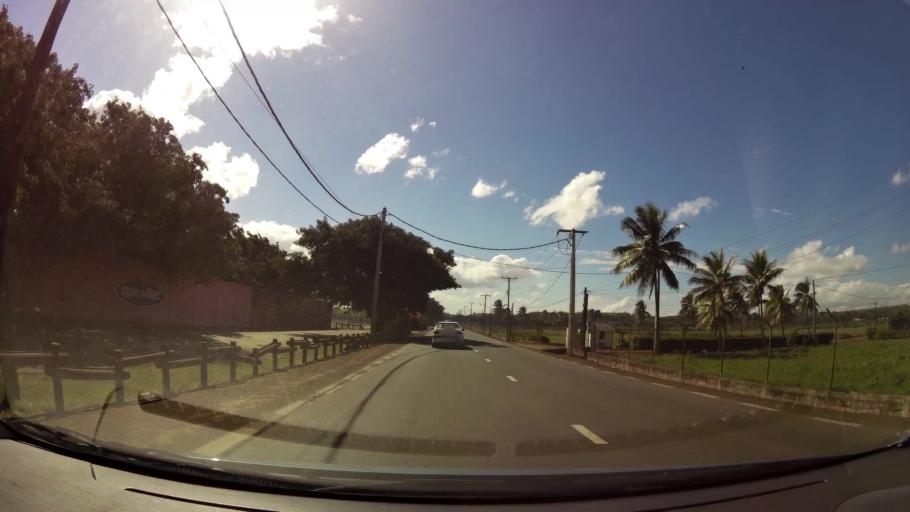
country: MU
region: Black River
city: Gros Cailloux
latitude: -20.2465
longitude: 57.4213
